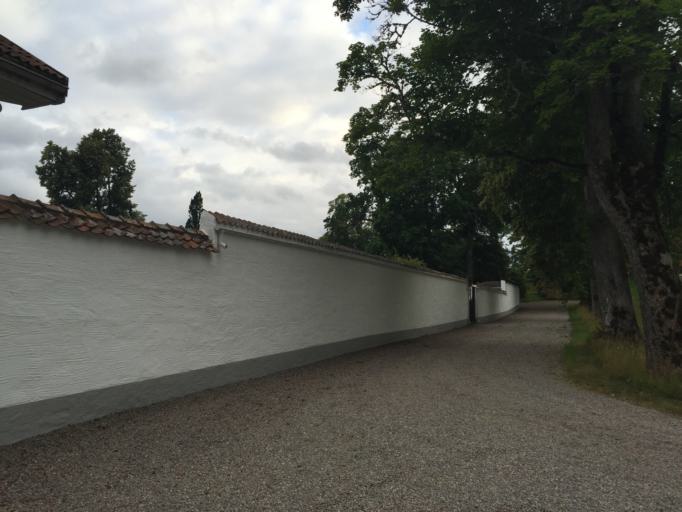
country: SE
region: OErebro
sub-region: Hallsbergs Kommun
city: Palsboda
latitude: 58.9261
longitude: 15.5216
